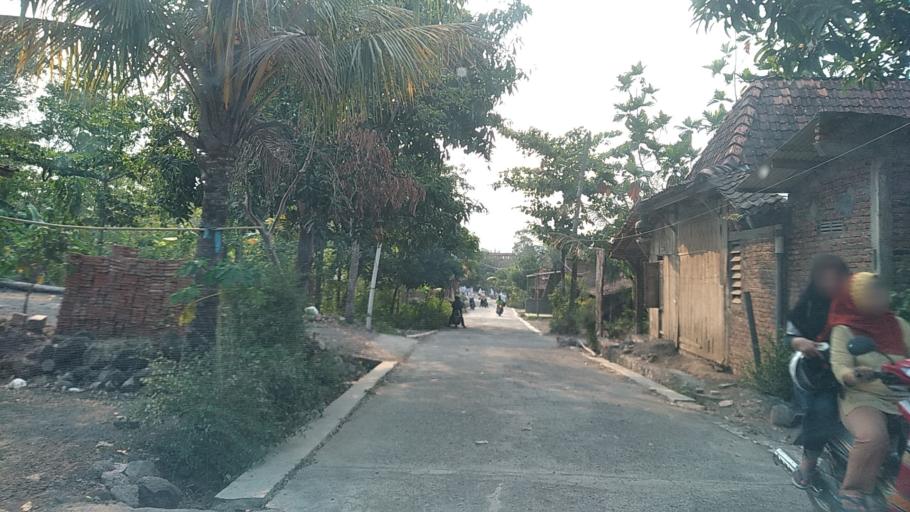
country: ID
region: Central Java
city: Mranggen
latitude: -7.0628
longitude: 110.4843
